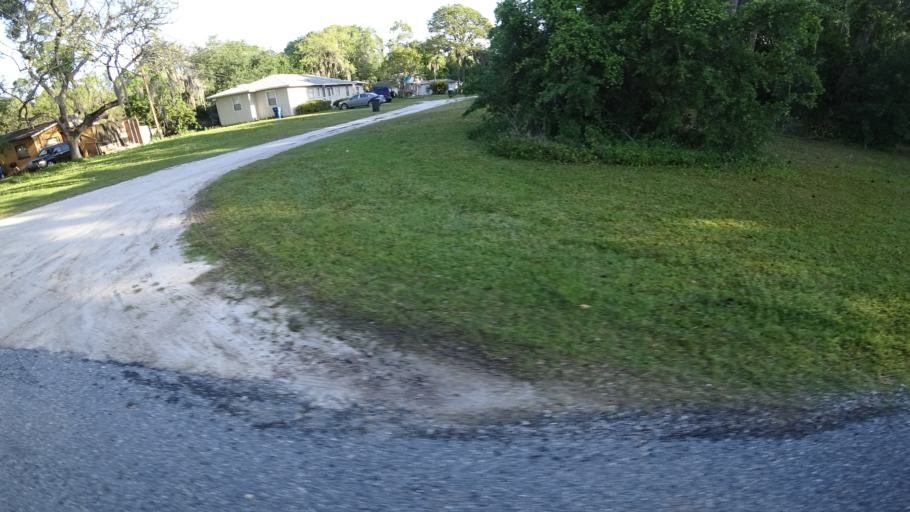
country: US
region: Florida
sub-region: Manatee County
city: Samoset
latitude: 27.4437
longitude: -82.5393
